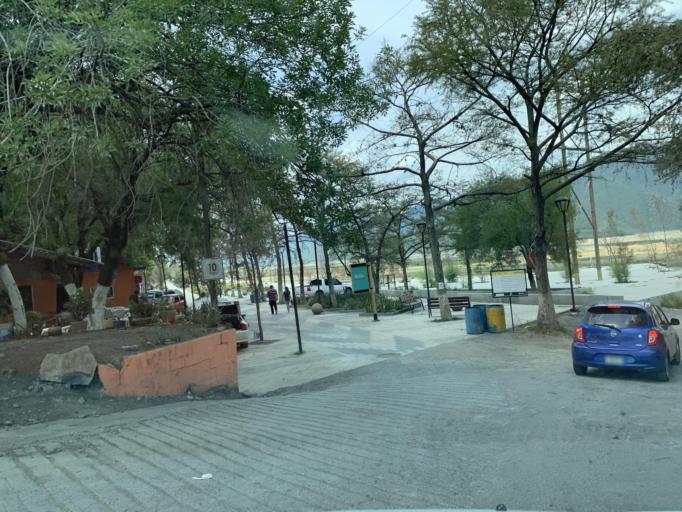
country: MX
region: Nuevo Leon
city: Santiago
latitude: 25.4104
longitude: -100.1374
